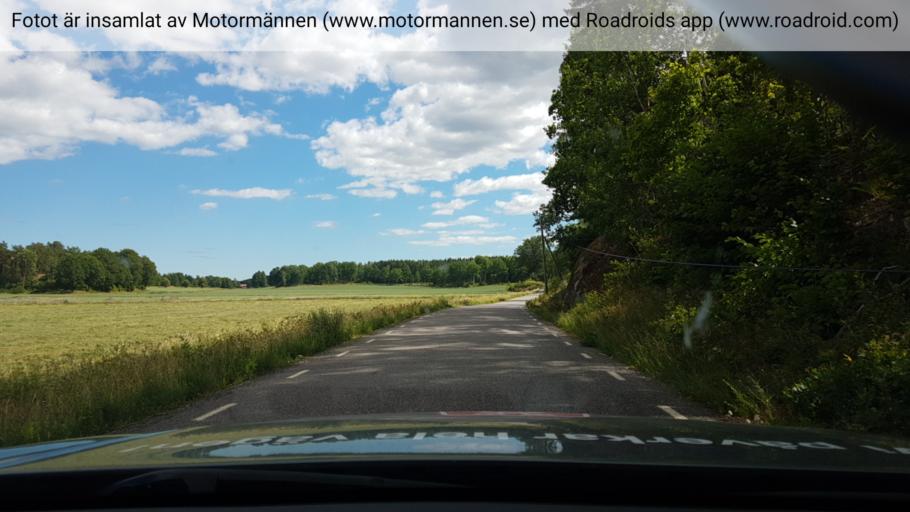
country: SE
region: Kalmar
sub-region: Vasterviks Kommun
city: Forserum
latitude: 57.9744
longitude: 16.6145
